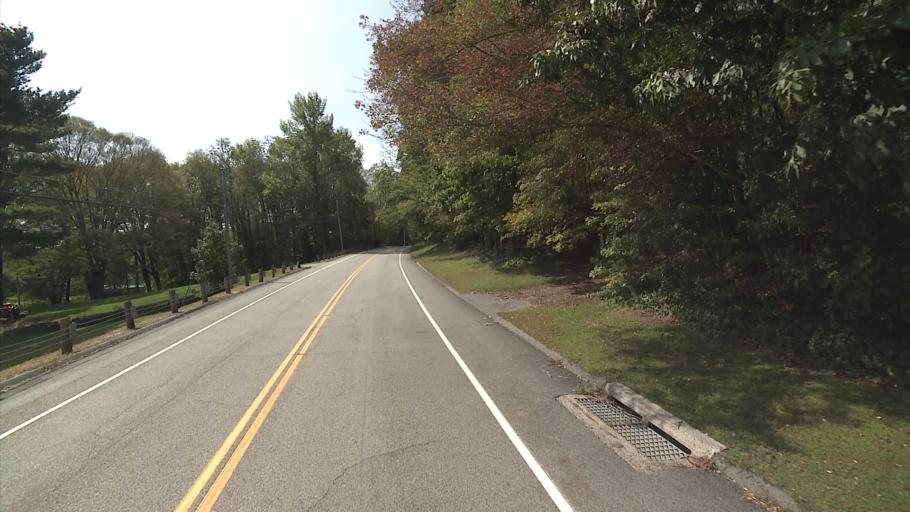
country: US
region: Connecticut
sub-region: Windham County
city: Wauregan
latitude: 41.7400
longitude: -71.9616
